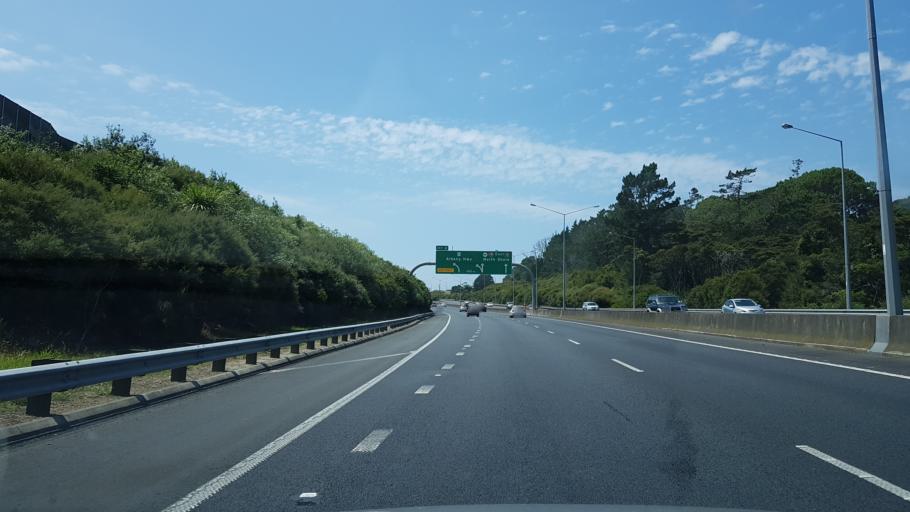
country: NZ
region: Auckland
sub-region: Auckland
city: Rothesay Bay
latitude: -36.7633
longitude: 174.6975
